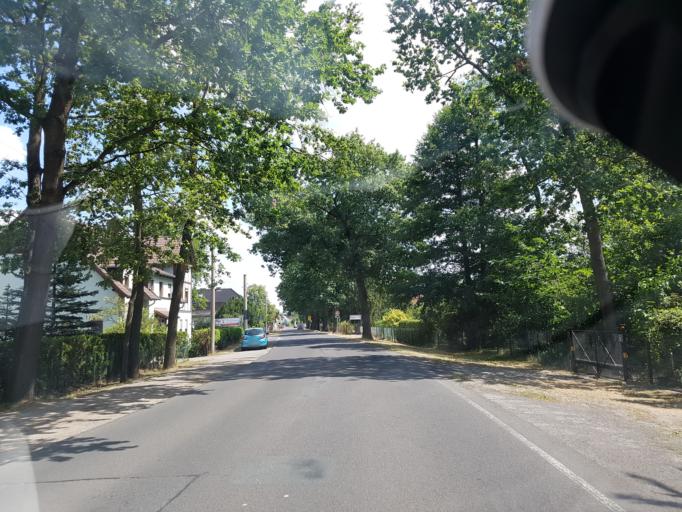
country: DE
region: Brandenburg
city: Cottbus
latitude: 51.7208
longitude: 14.3597
